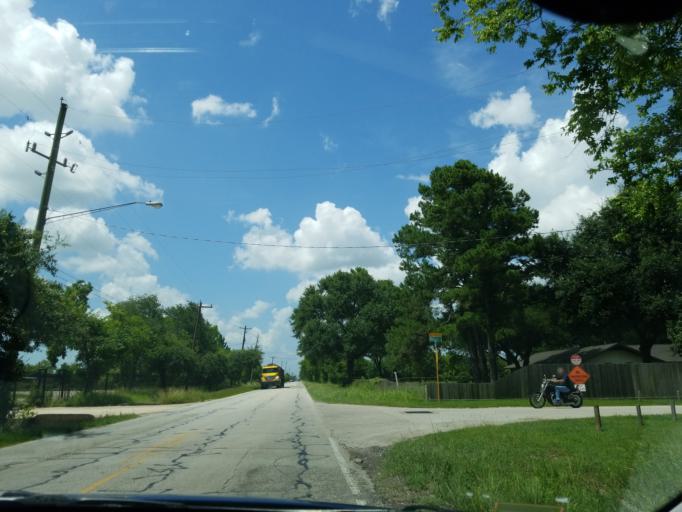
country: US
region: Texas
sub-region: Harris County
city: Katy
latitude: 29.8658
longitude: -95.8071
